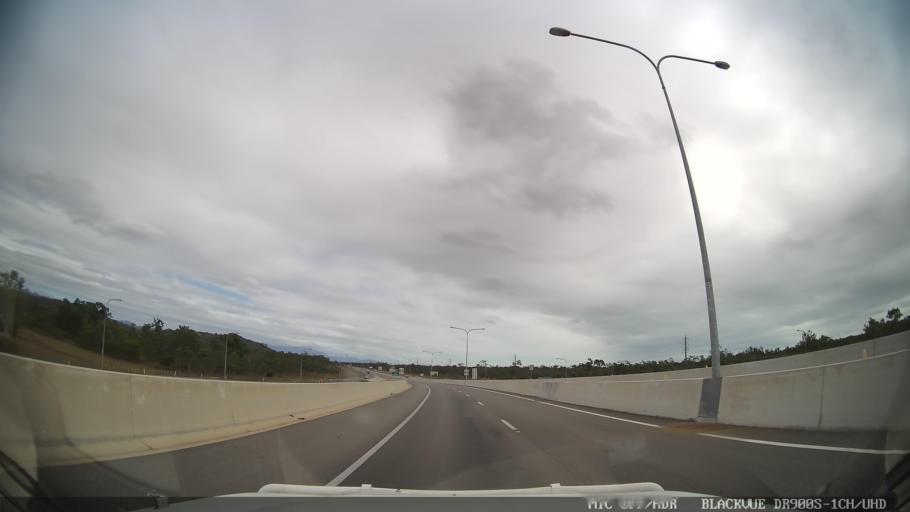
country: AU
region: Queensland
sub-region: Townsville
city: Bohle Plains
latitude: -19.2401
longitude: 146.6630
